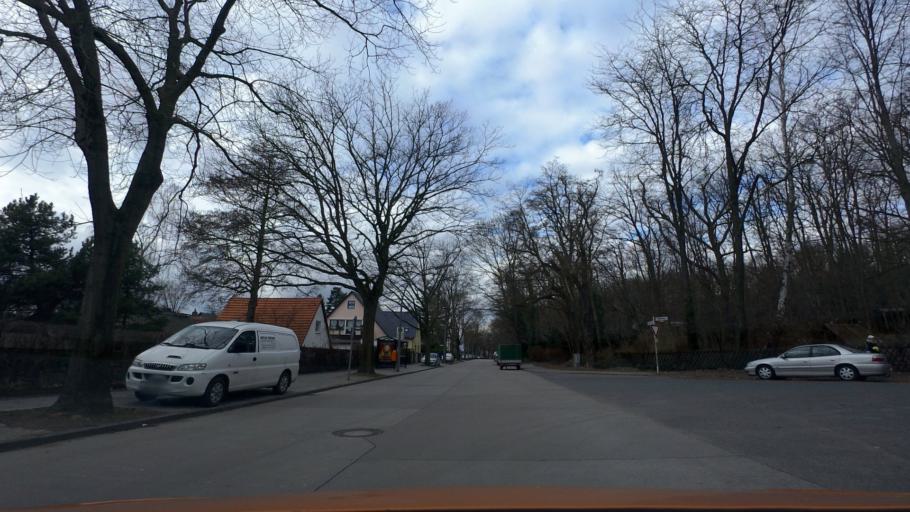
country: DE
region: Berlin
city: Konradshohe
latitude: 52.5961
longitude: 13.2195
